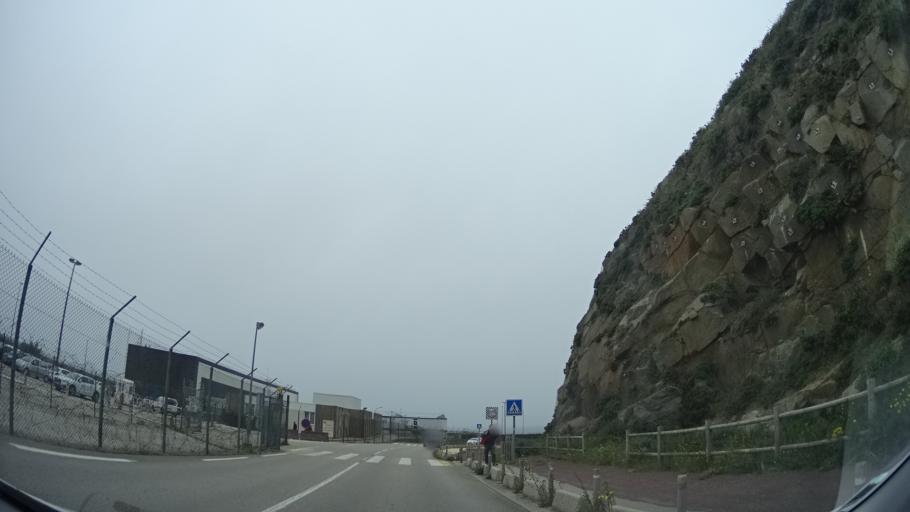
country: FR
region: Lower Normandy
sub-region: Departement de la Manche
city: Flamanville
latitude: 49.5436
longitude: -1.8735
